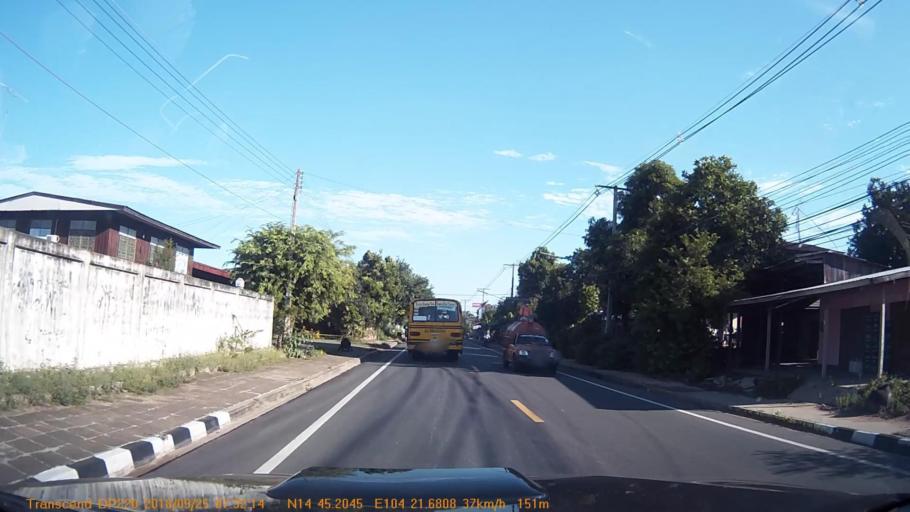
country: TH
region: Sisaket
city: Phrai Bueng
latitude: 14.7536
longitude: 104.3613
